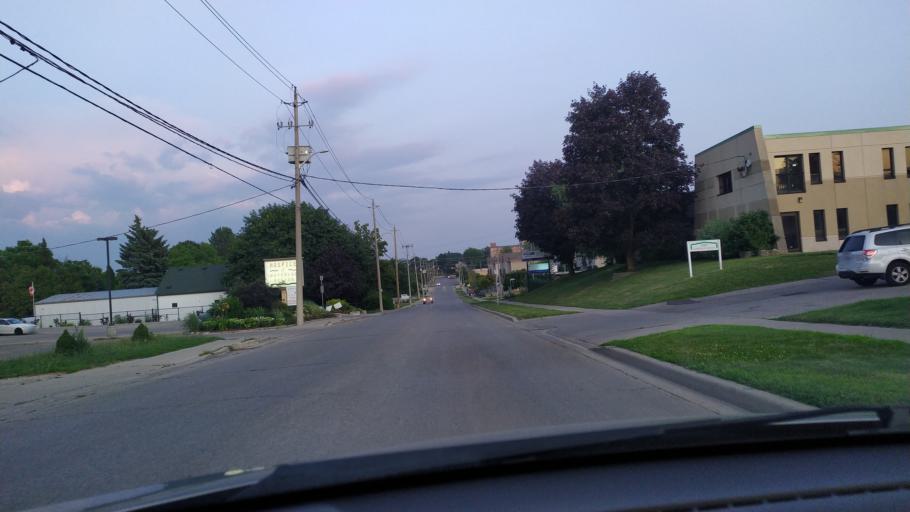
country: CA
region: Ontario
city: Kitchener
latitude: 43.4416
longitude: -80.5139
